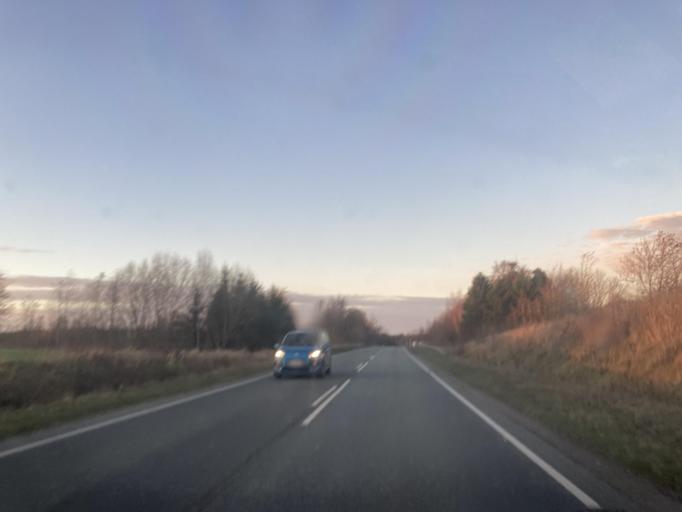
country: DK
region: Capital Region
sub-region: Gribskov Kommune
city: Graested
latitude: 56.0559
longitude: 12.2760
